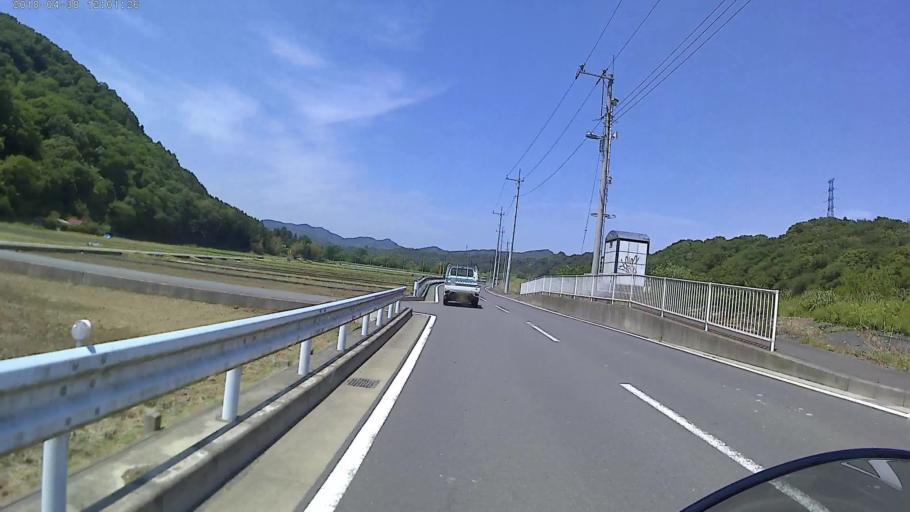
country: JP
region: Kanagawa
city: Zama
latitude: 35.5173
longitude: 139.3254
